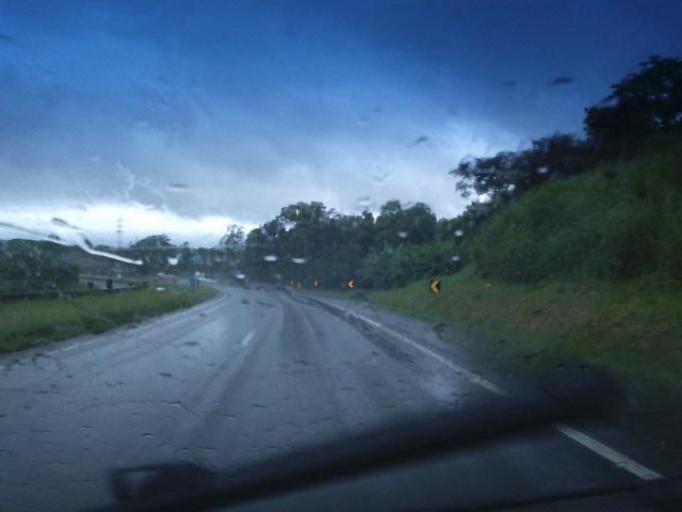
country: BR
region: Sao Paulo
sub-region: Miracatu
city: Miracatu
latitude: -24.2634
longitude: -47.3807
